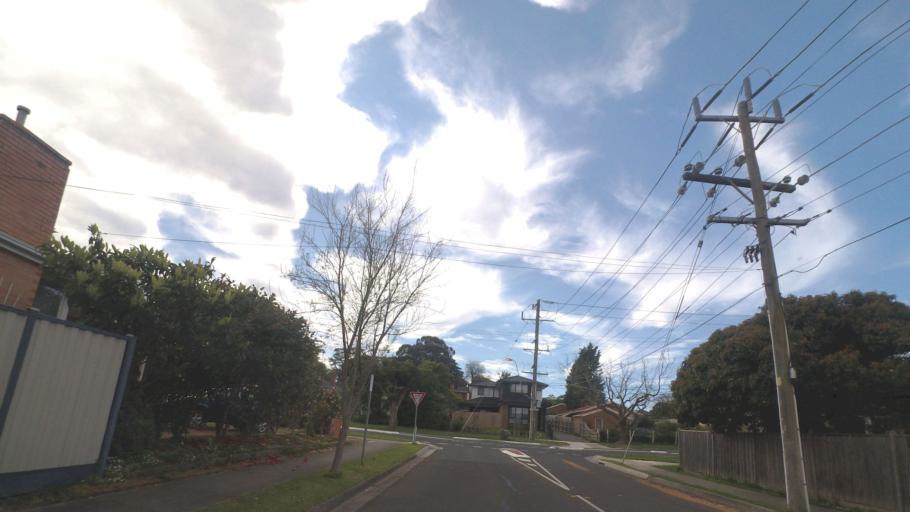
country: AU
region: Victoria
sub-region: Knox
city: Bayswater
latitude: -37.8477
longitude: 145.2609
